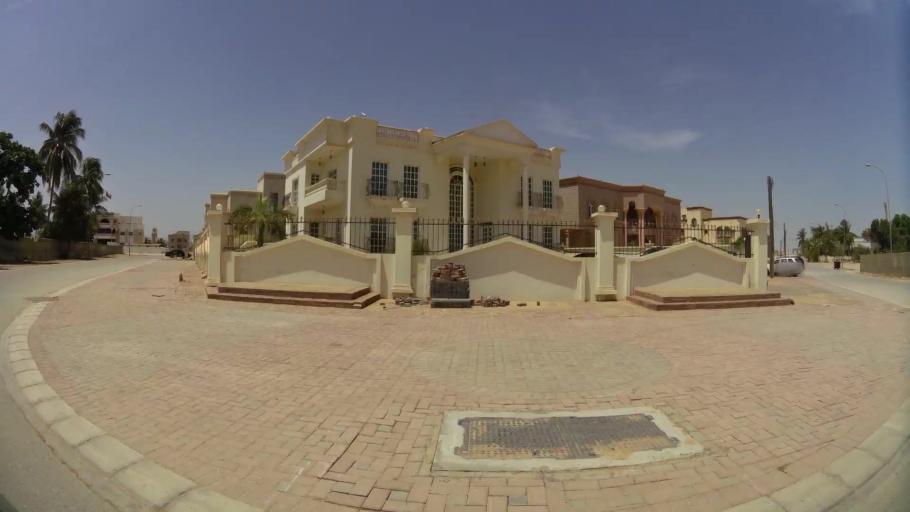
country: OM
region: Zufar
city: Salalah
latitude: 17.0638
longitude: 54.1509
